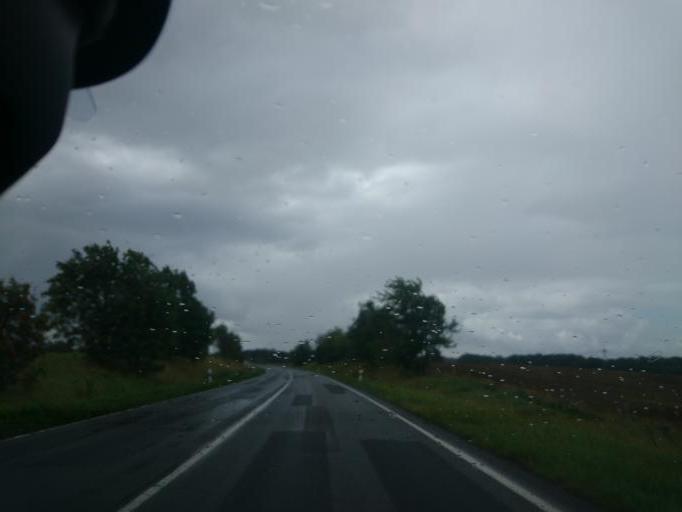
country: DE
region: Mecklenburg-Vorpommern
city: Bergen auf Ruegen
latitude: 54.4211
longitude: 13.4054
